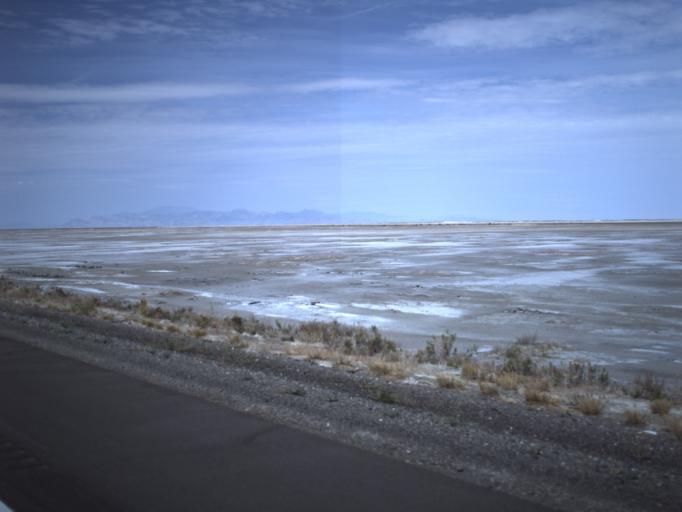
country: US
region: Utah
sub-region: Tooele County
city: Wendover
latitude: 40.7281
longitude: -113.3018
